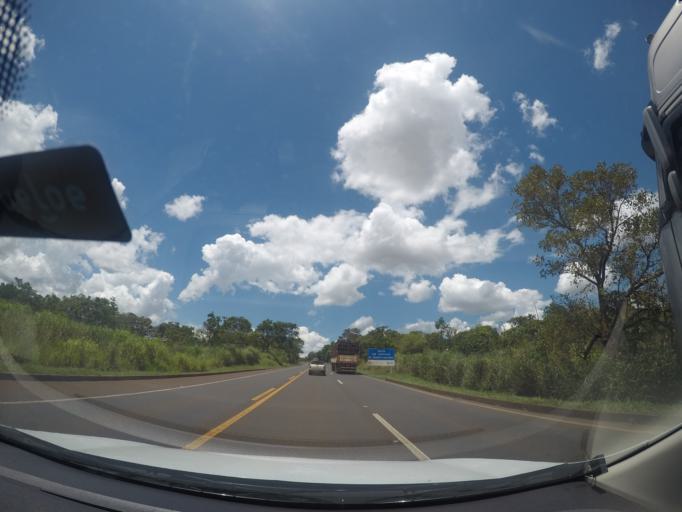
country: BR
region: Minas Gerais
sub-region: Monte Alegre De Minas
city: Monte Alegre de Minas
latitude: -18.8901
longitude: -49.0496
